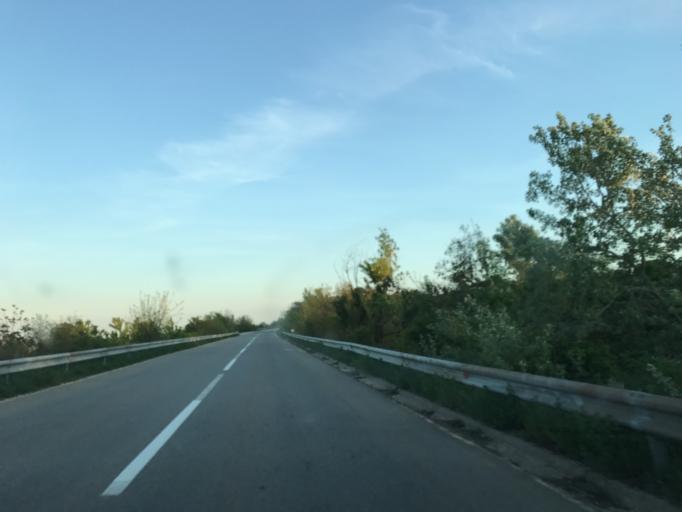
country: RO
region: Mehedinti
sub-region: Comuna Gogosu
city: Ostrovu Mare
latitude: 44.4185
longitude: 22.4833
